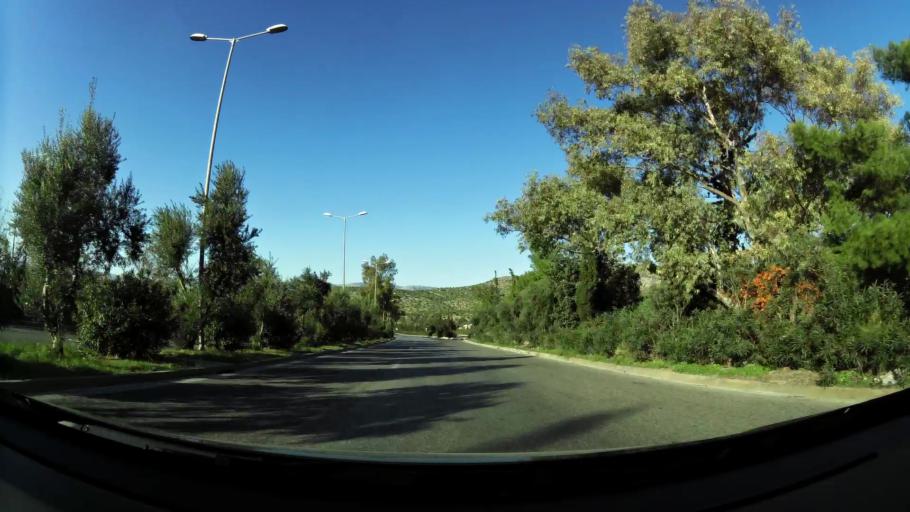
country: GR
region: Attica
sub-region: Nomarchia Athinas
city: Skaramangas
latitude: 38.0046
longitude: 23.6039
